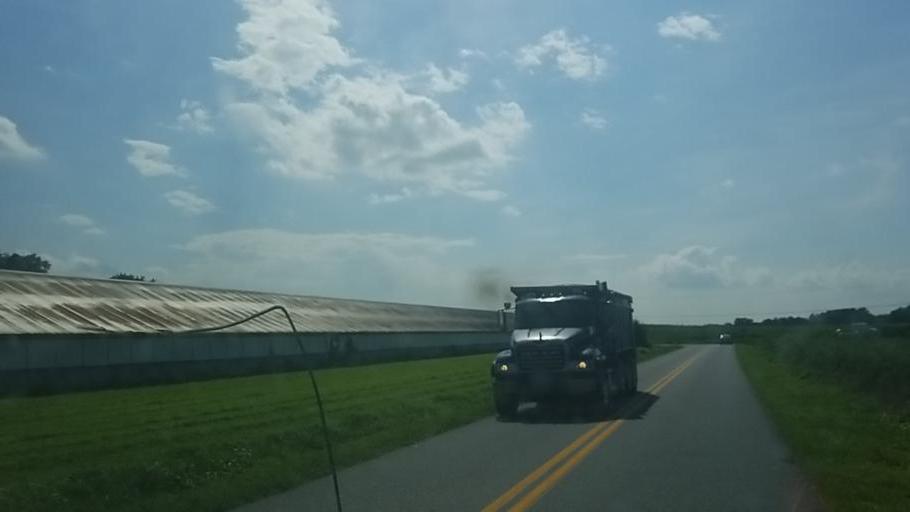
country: US
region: Maryland
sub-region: Somerset County
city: Princess Anne
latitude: 38.2613
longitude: -75.6803
